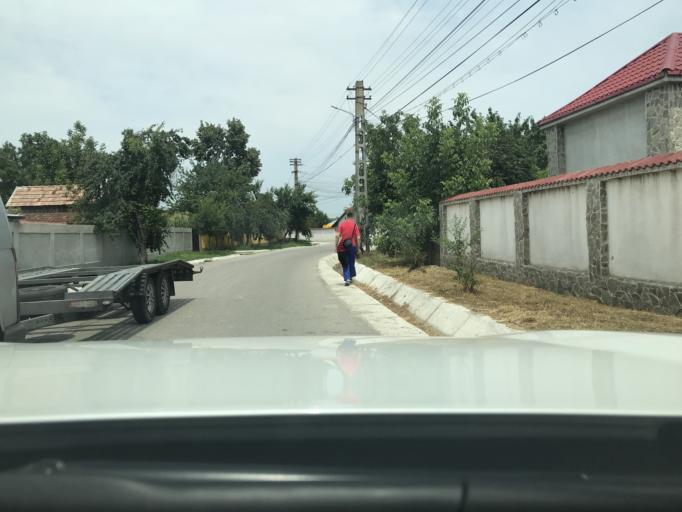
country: RO
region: Olt
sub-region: Comuna Osica de Sus
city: Osica de Sus
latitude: 44.2564
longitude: 24.3152
